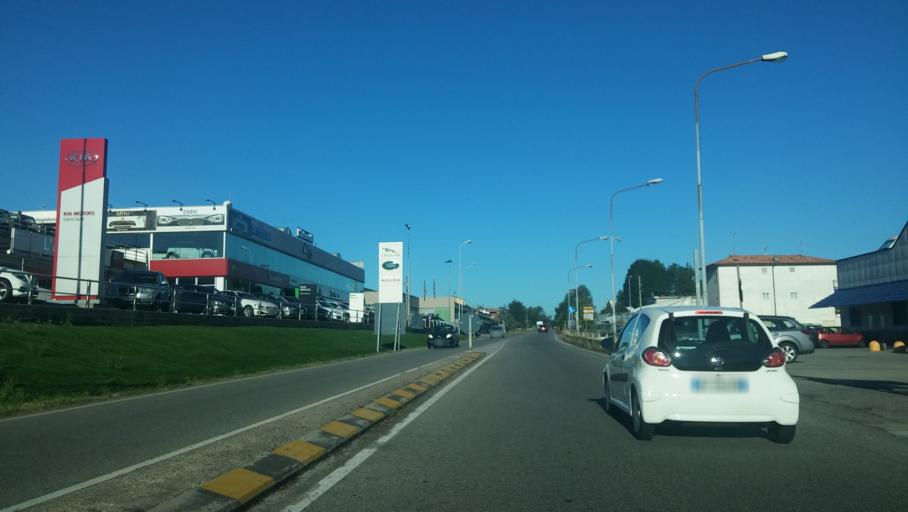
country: IT
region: Lombardy
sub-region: Provincia di Como
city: Montorfano
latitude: 45.7946
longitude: 9.1481
